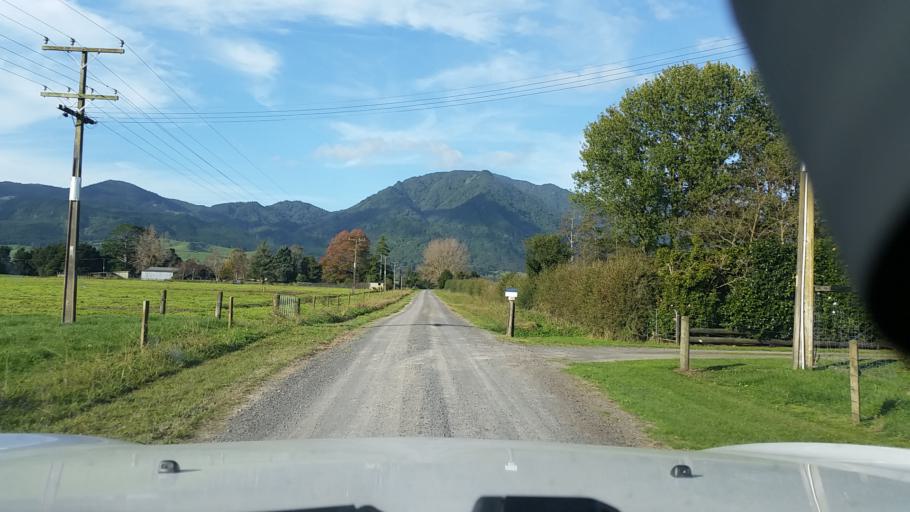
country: NZ
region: Waikato
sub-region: Matamata-Piako District
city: Matamata
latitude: -37.6588
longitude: 175.7912
